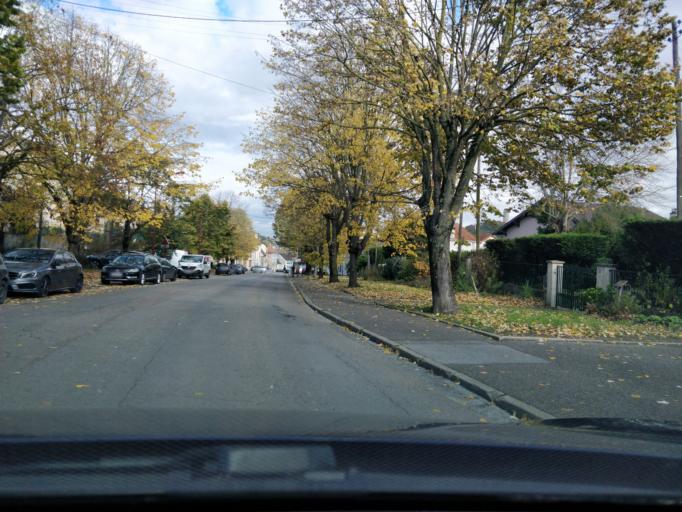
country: FR
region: Ile-de-France
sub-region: Departement de l'Essonne
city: Linas
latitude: 48.6272
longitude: 2.2632
